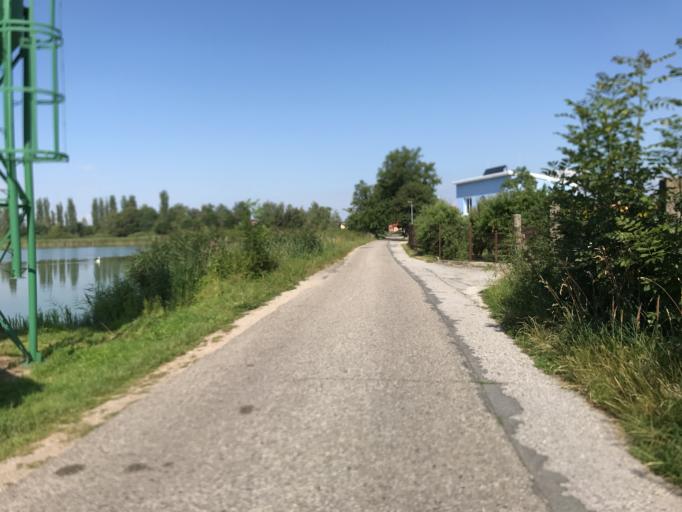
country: CZ
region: Jihocesky
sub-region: Okres Jindrichuv Hradec
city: Trebon
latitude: 49.0158
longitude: 14.7420
